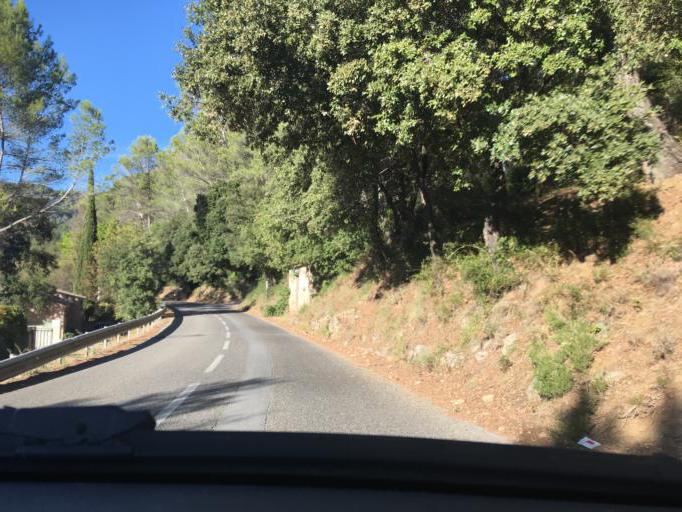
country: FR
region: Provence-Alpes-Cote d'Azur
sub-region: Departement du Var
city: Flayosc
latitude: 43.5722
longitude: 6.4240
